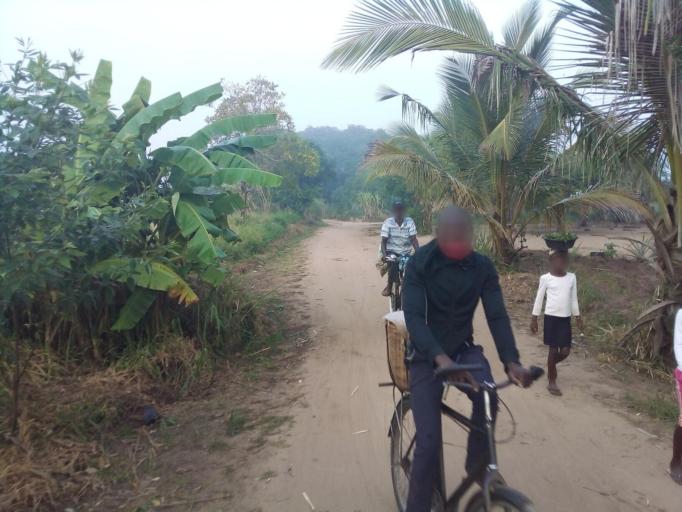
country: MZ
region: Zambezia
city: Quelimane
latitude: -17.5851
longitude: 36.6888
